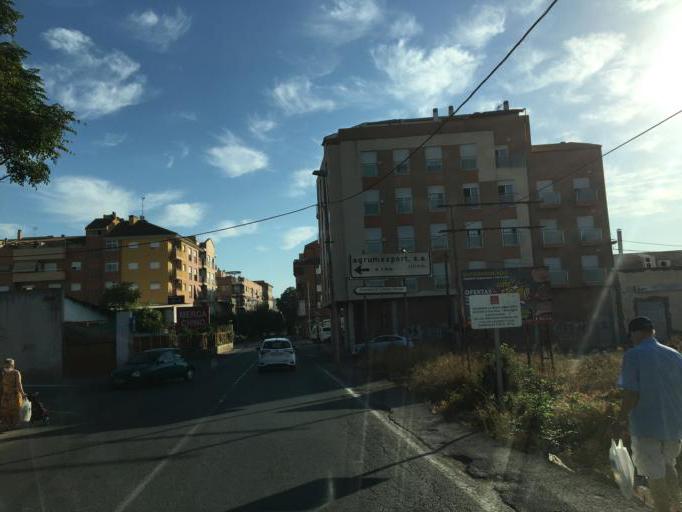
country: ES
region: Murcia
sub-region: Murcia
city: Murcia
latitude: 38.0236
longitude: -1.1319
